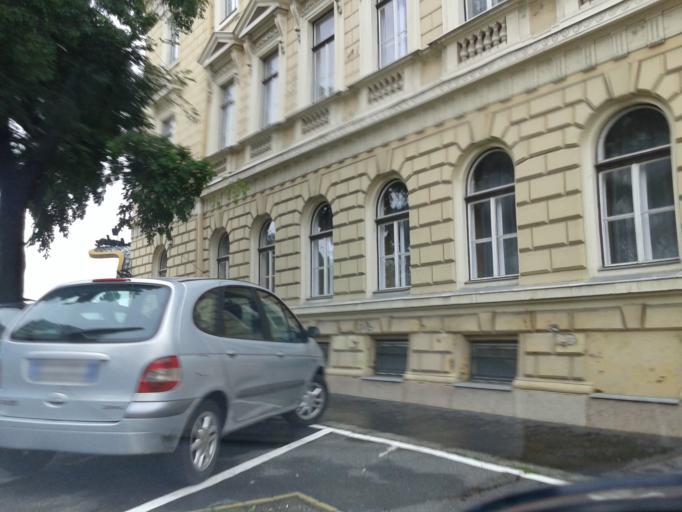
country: HU
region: Csongrad
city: Szeged
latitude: 46.2558
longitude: 20.1561
